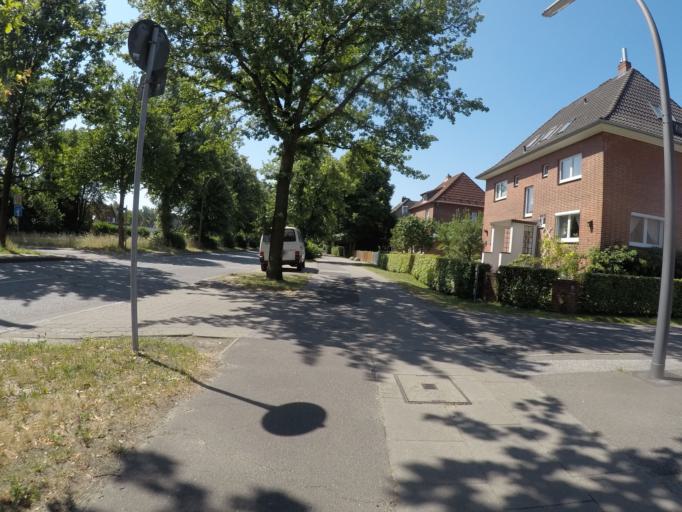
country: DE
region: Hamburg
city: Rothenburgsort
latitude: 53.4967
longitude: 10.0228
